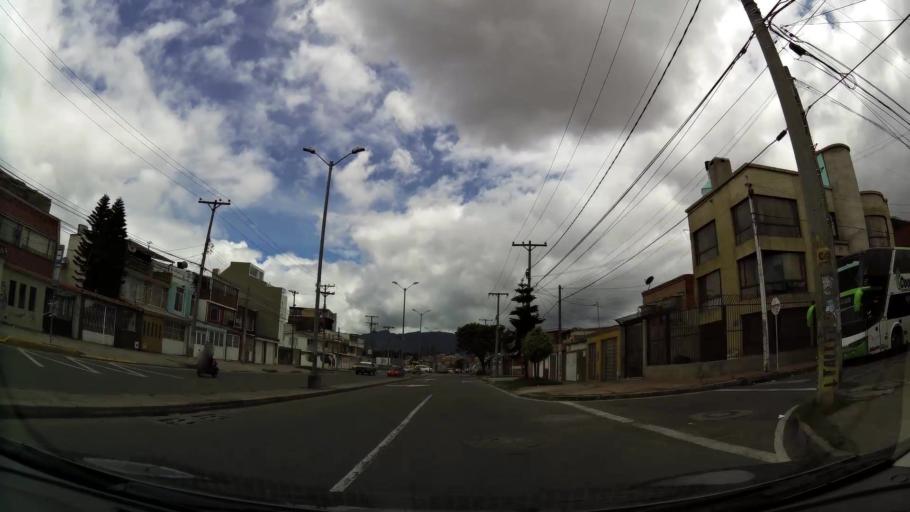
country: CO
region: Bogota D.C.
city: Barrio San Luis
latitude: 4.7082
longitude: -74.0926
